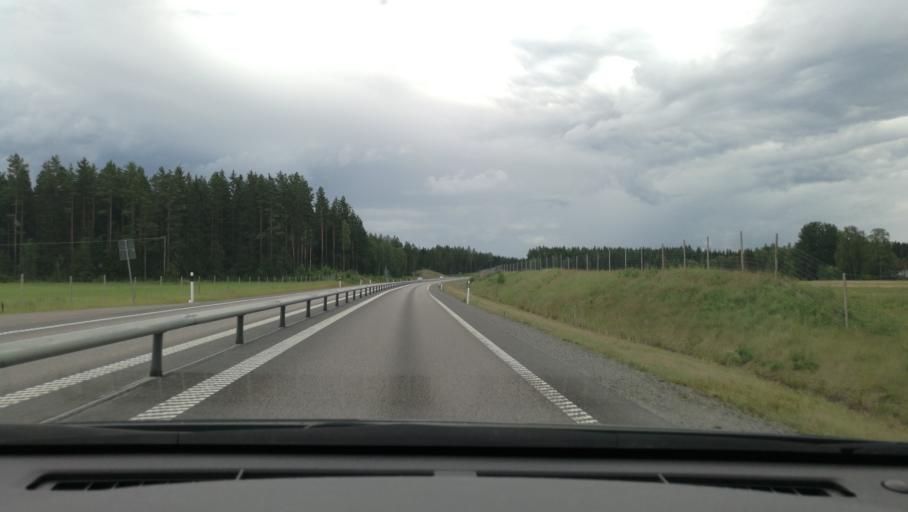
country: SE
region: Soedermanland
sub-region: Katrineholms Kommun
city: Katrineholm
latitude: 58.9849
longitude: 16.2658
